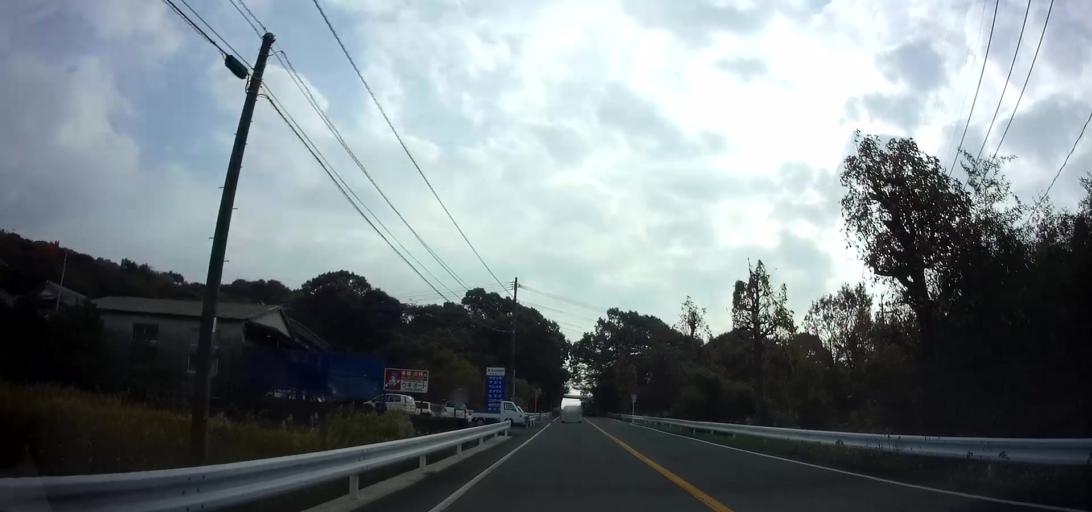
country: JP
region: Nagasaki
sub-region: Isahaya-shi
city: Isahaya
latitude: 32.7964
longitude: 130.0940
